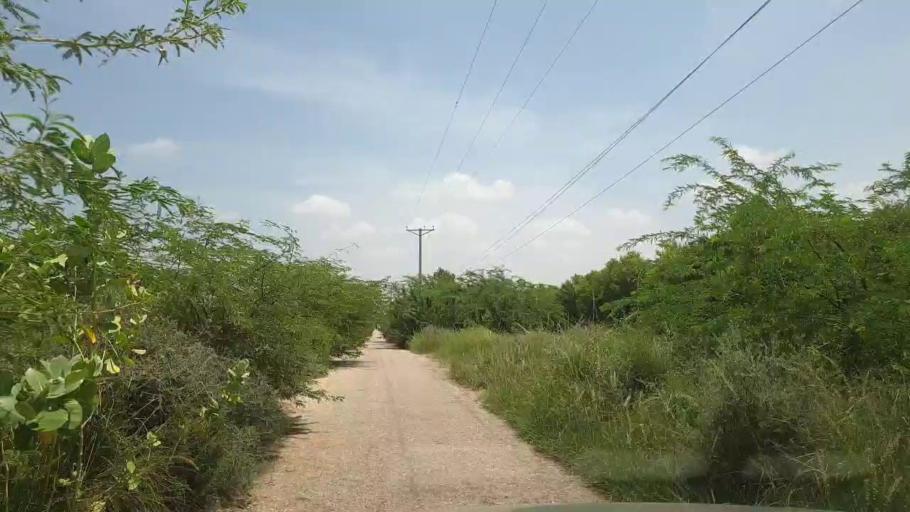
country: PK
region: Sindh
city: Kot Diji
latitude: 27.1294
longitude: 69.0017
